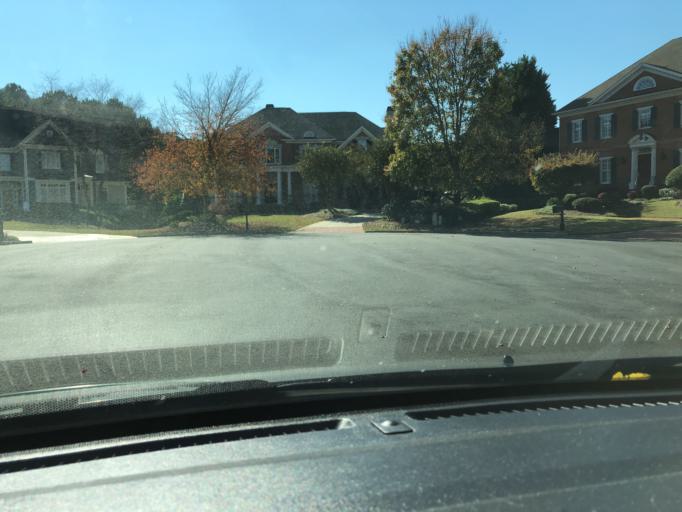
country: US
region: Georgia
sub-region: Gwinnett County
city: Berkeley Lake
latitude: 33.9936
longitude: -84.1986
